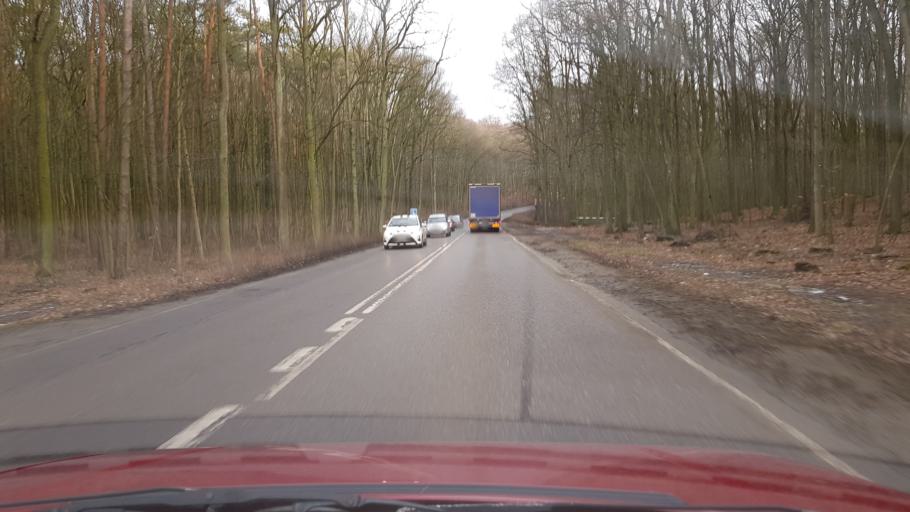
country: PL
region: West Pomeranian Voivodeship
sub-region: Powiat policki
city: Police
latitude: 53.5226
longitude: 14.5686
